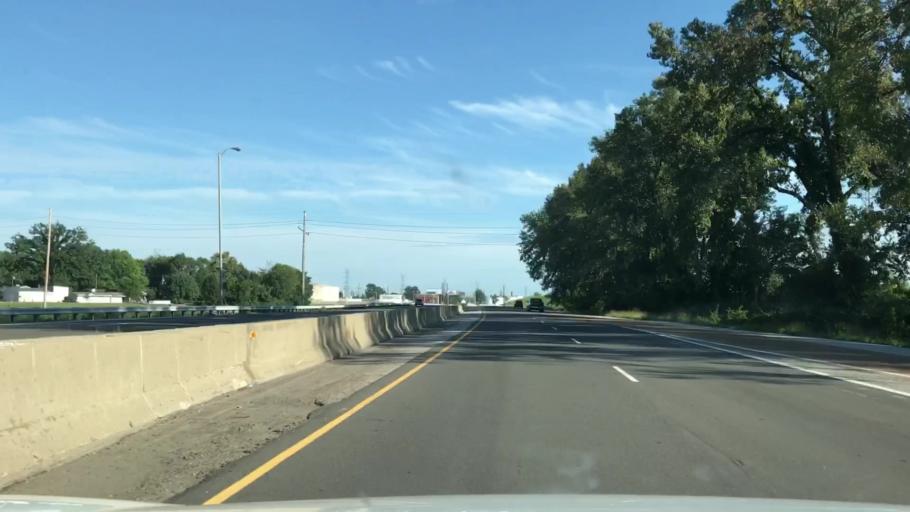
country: US
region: Illinois
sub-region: Madison County
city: Wood River
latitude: 38.8566
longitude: -90.1075
